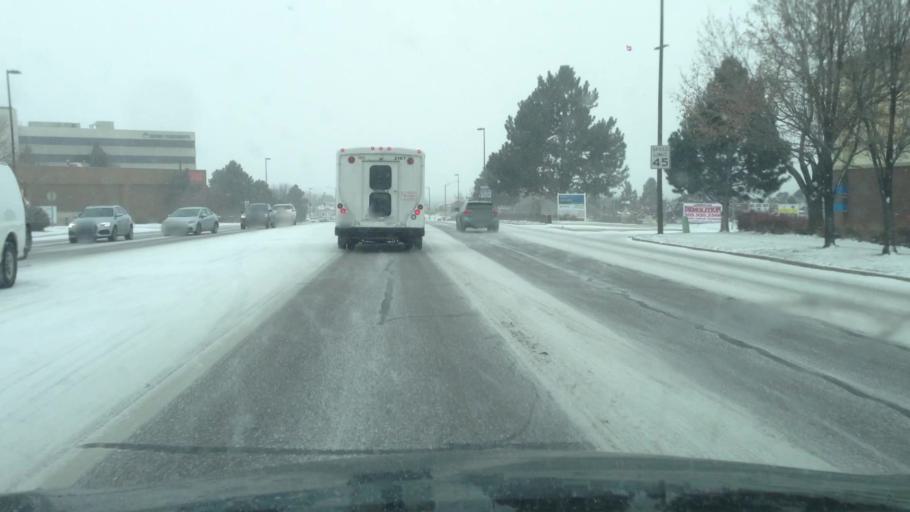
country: US
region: Colorado
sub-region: Adams County
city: Aurora
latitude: 39.6738
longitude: -104.8660
